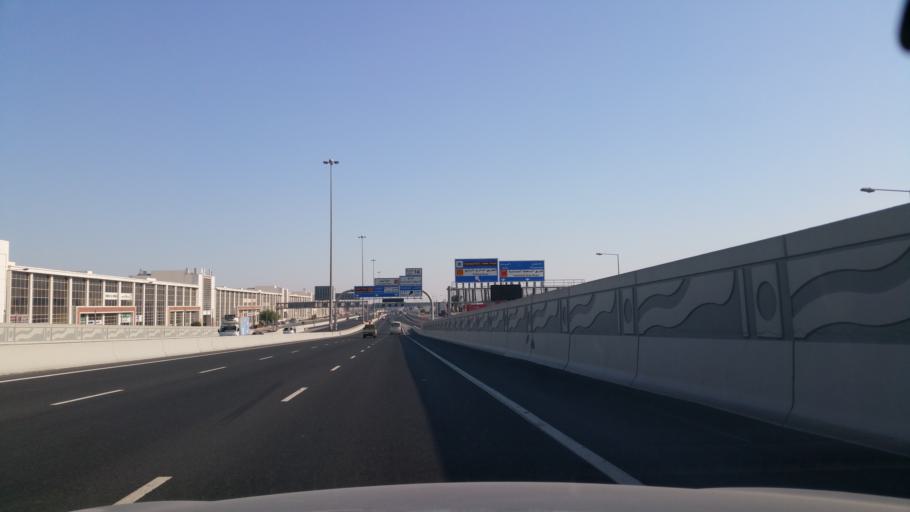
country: QA
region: Baladiyat ar Rayyan
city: Ar Rayyan
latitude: 25.2017
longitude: 51.4489
